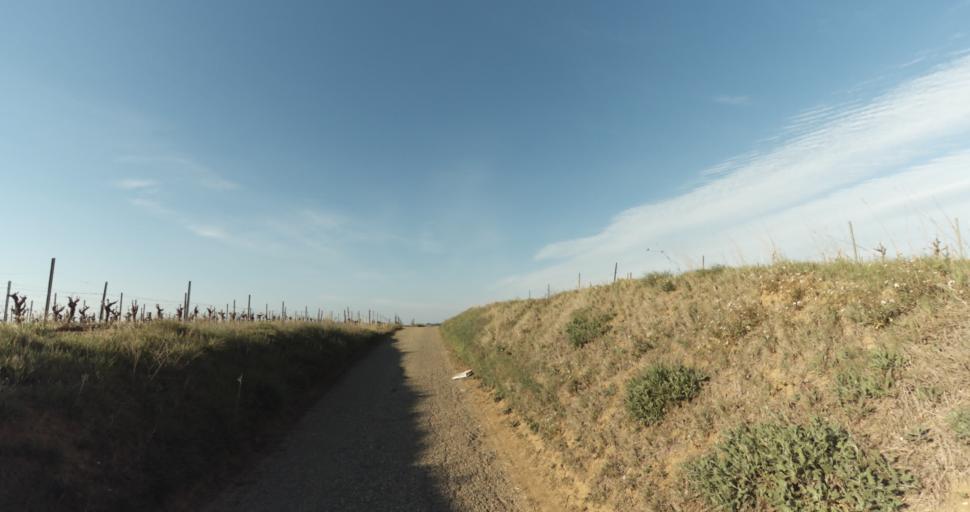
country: FR
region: Languedoc-Roussillon
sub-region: Departement de l'Herault
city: Marseillan
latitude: 43.3632
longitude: 3.5111
